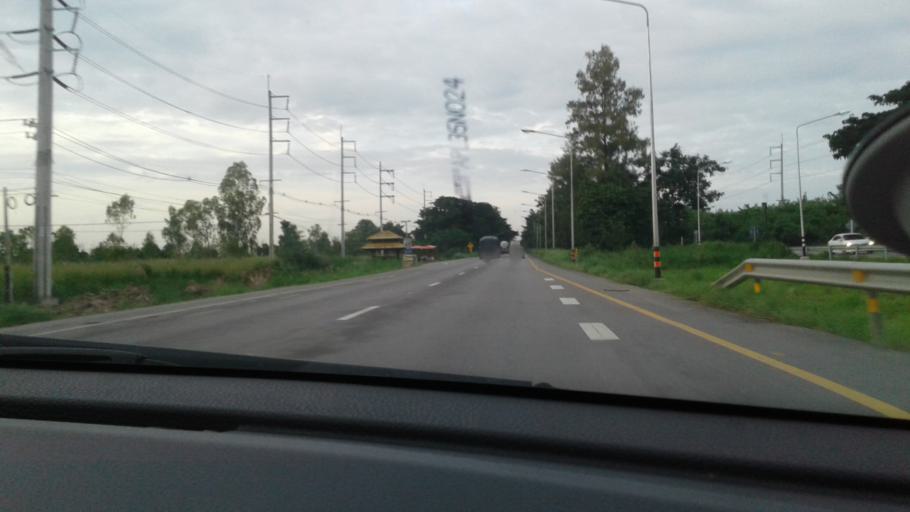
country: TH
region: Prachuap Khiri Khan
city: Hua Hin
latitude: 12.5176
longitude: 99.8822
